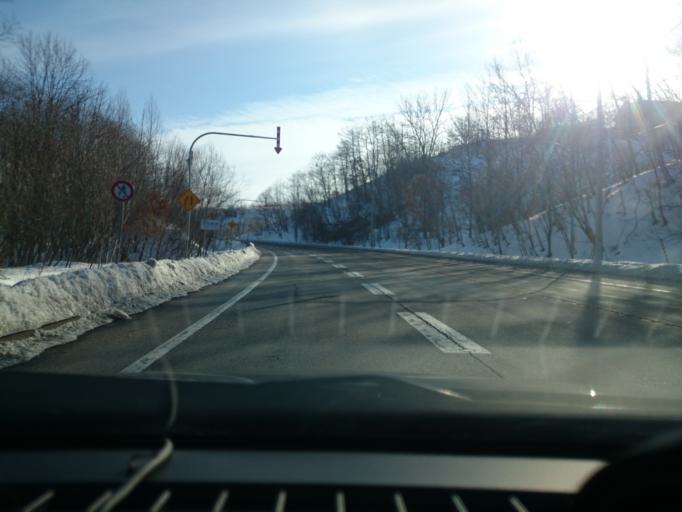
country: JP
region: Hokkaido
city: Otofuke
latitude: 43.2303
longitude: 143.5264
